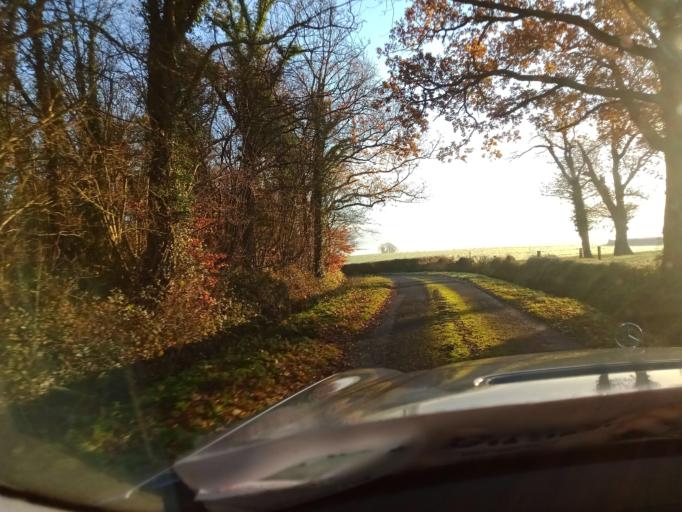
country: IE
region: Leinster
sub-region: Kilkenny
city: Callan
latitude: 52.5294
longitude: -7.4488
